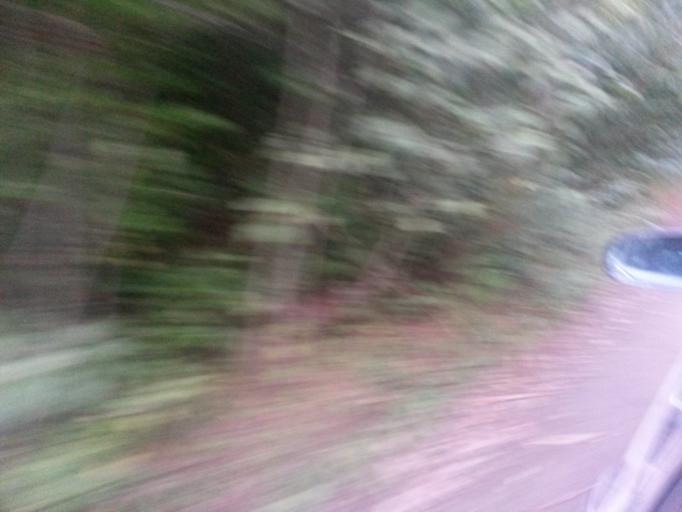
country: RO
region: Alba
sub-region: Comuna Ponor
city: Ponor
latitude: 46.3116
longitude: 23.4008
